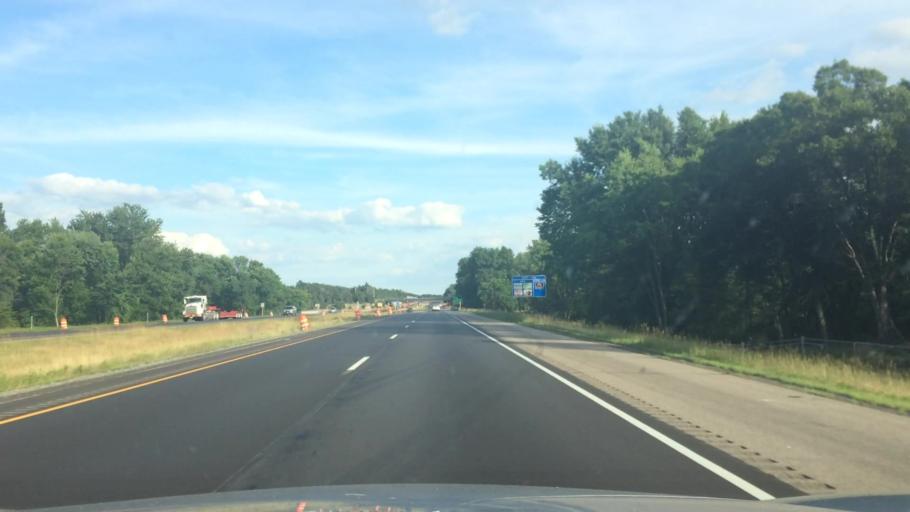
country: US
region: Wisconsin
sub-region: Portage County
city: Stevens Point
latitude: 44.5288
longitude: -89.5330
